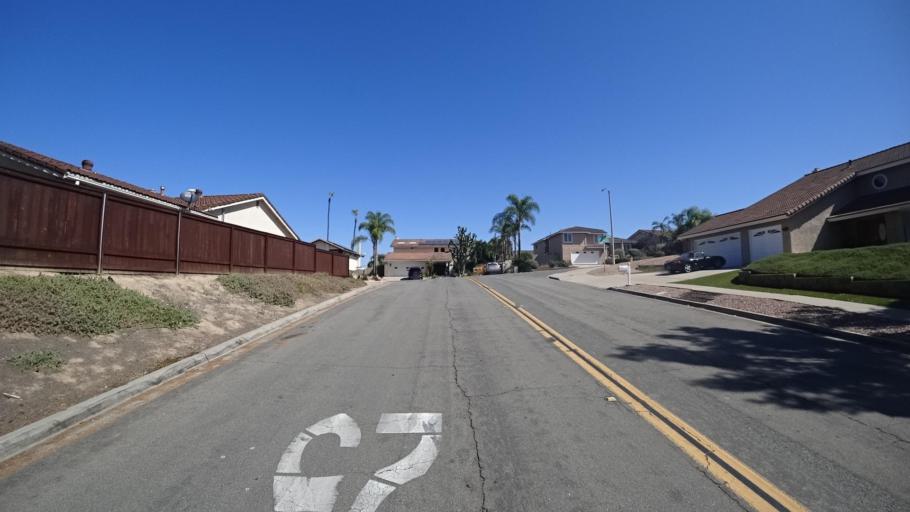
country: US
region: California
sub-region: San Diego County
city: Bonita
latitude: 32.6692
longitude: -117.0012
